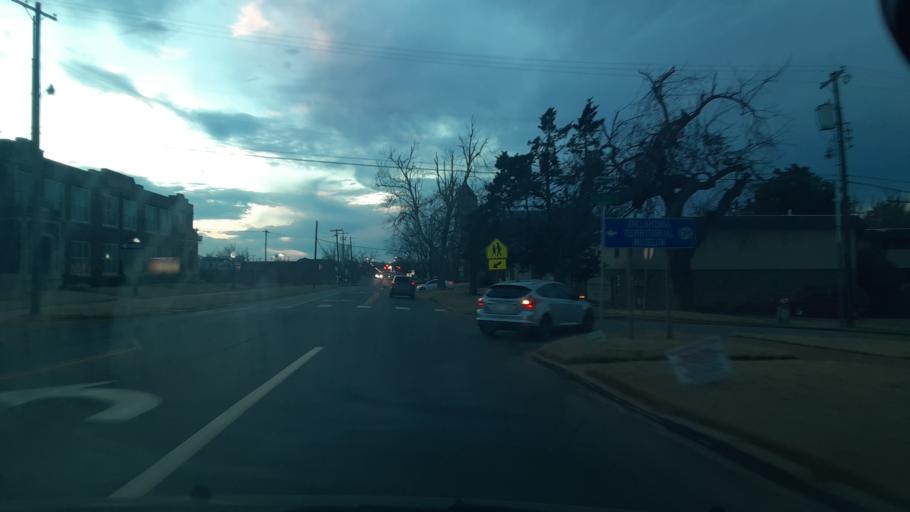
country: US
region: Oklahoma
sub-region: Logan County
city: Guthrie
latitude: 35.8802
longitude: -97.4213
